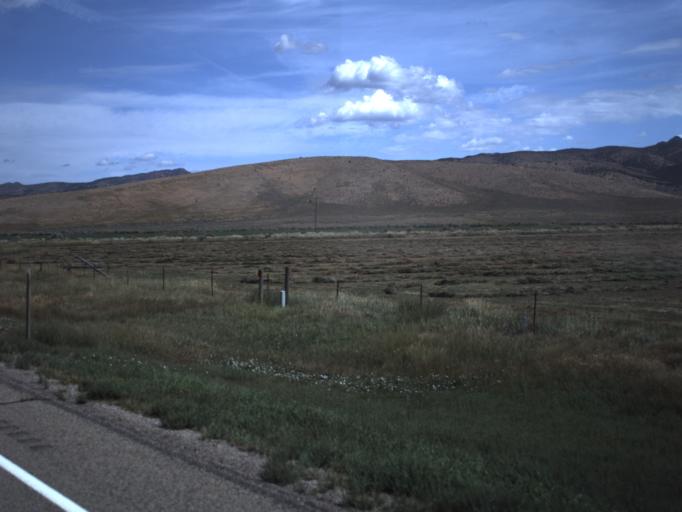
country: US
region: Utah
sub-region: Sanpete County
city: Fairview
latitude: 39.8033
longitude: -111.5025
